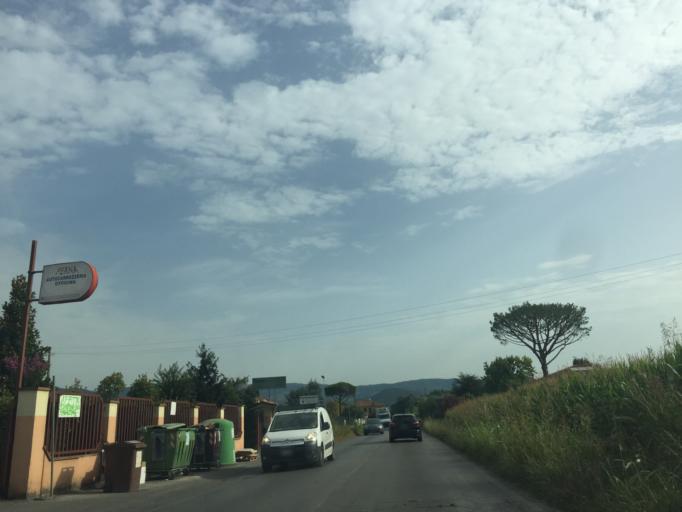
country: IT
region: Tuscany
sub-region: Provincia di Pistoia
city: Monsummano Terme
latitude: 43.8555
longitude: 10.7924
